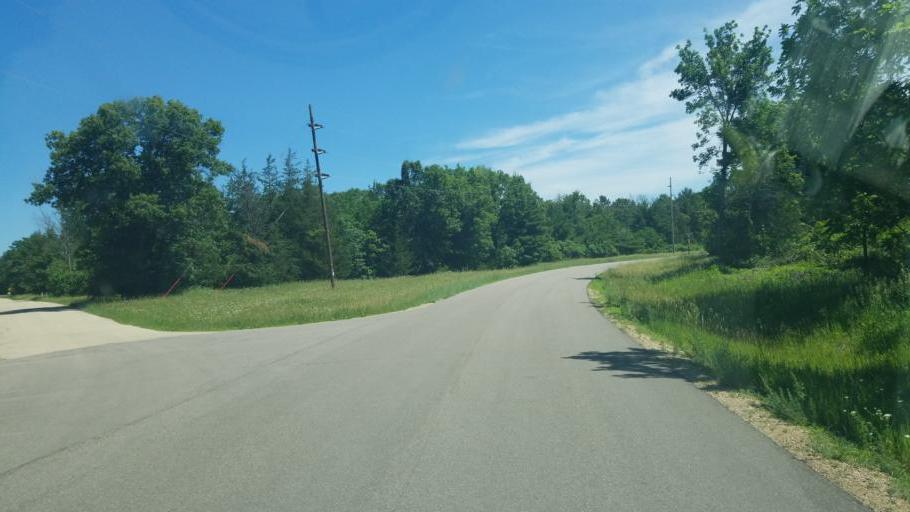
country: US
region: Wisconsin
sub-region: Juneau County
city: Mauston
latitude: 43.8684
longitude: -89.9484
